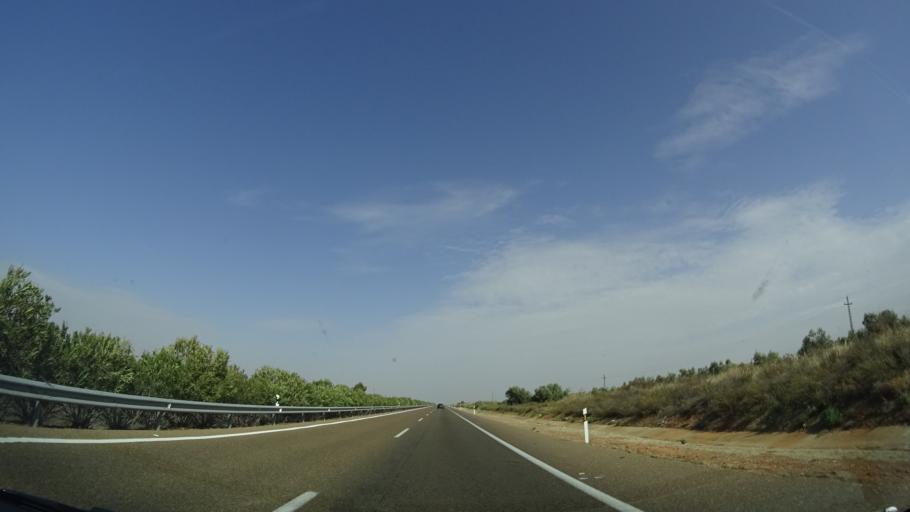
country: ES
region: Extremadura
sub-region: Provincia de Badajoz
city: Los Santos de Maimona
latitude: 38.5020
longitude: -6.3546
